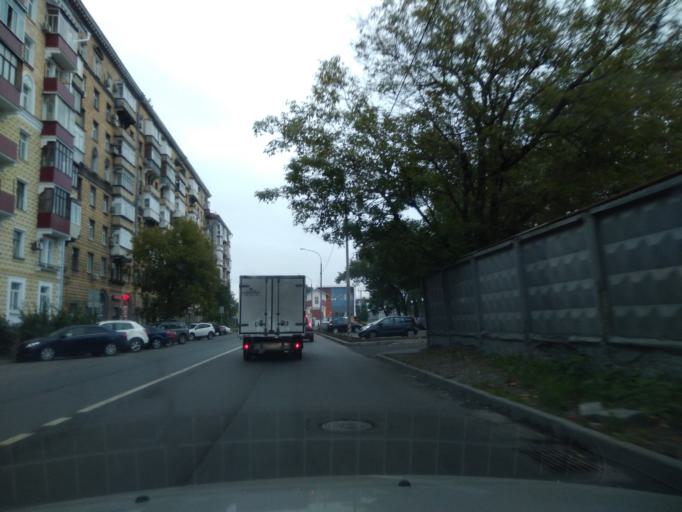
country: RU
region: Moscow
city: Sokol
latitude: 55.8000
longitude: 37.4988
